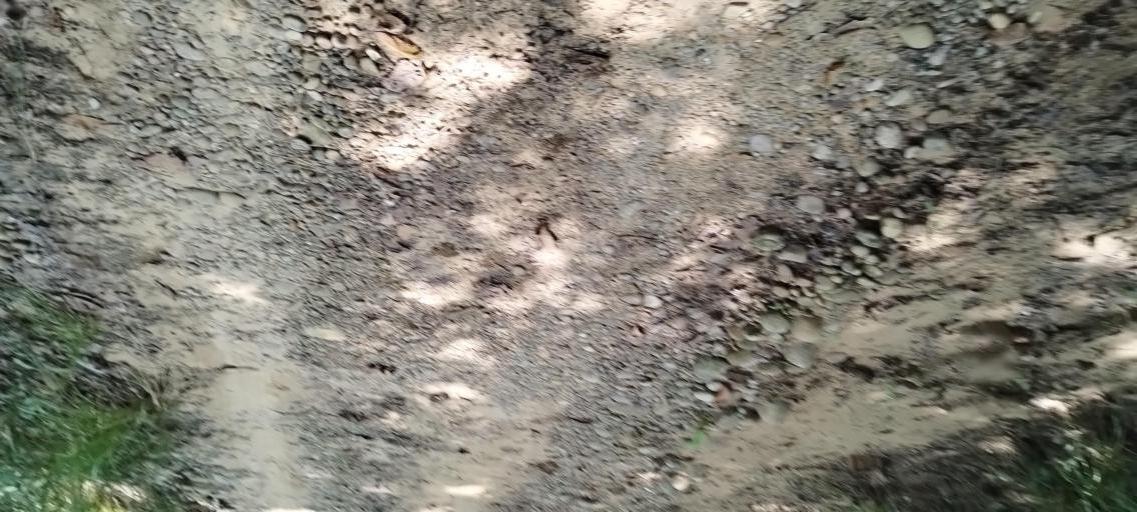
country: NP
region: Far Western
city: Tikapur
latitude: 28.4997
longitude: 81.2561
